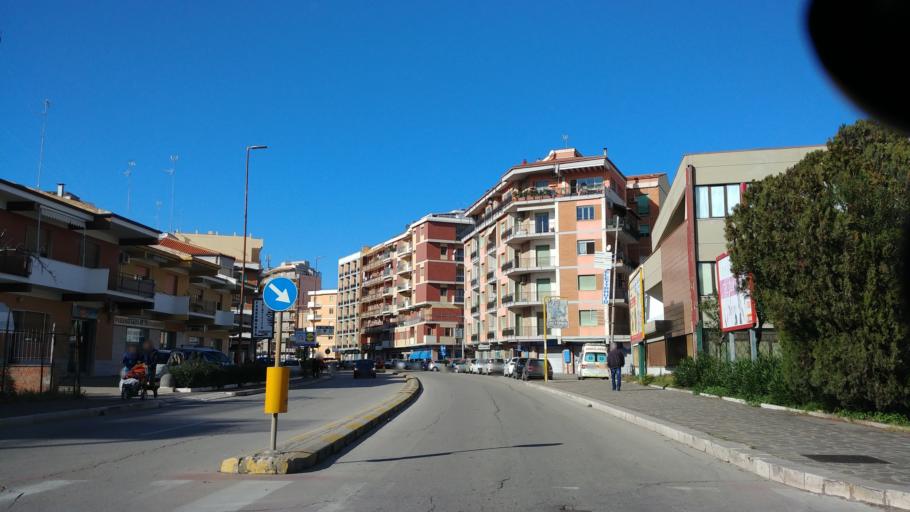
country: IT
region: Molise
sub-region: Provincia di Campobasso
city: Termoli
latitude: 41.9984
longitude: 14.9930
